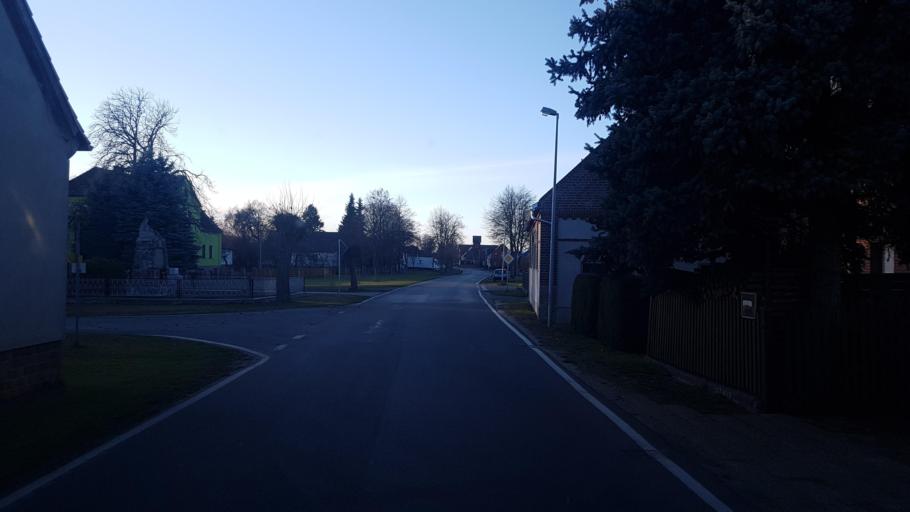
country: DE
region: Brandenburg
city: Drehnow
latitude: 51.8661
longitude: 14.3636
